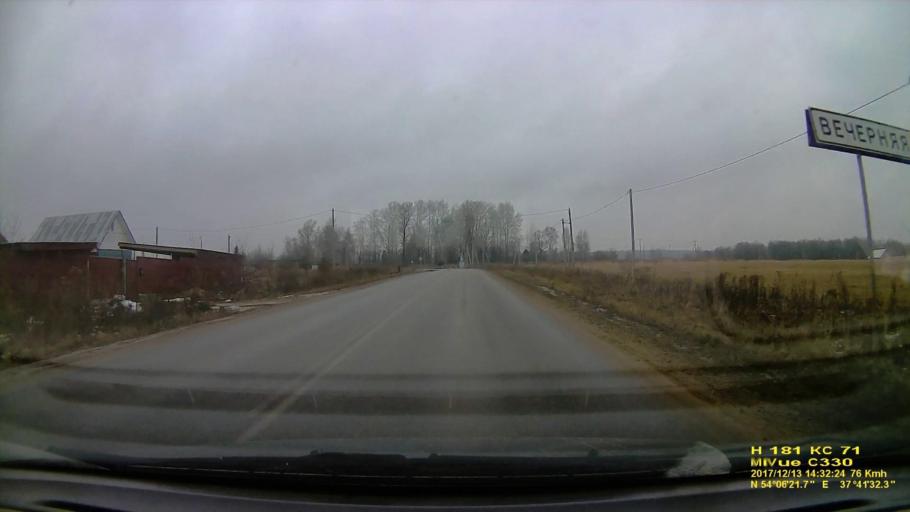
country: RU
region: Tula
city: Skuratovskiy
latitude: 54.1062
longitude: 37.6923
